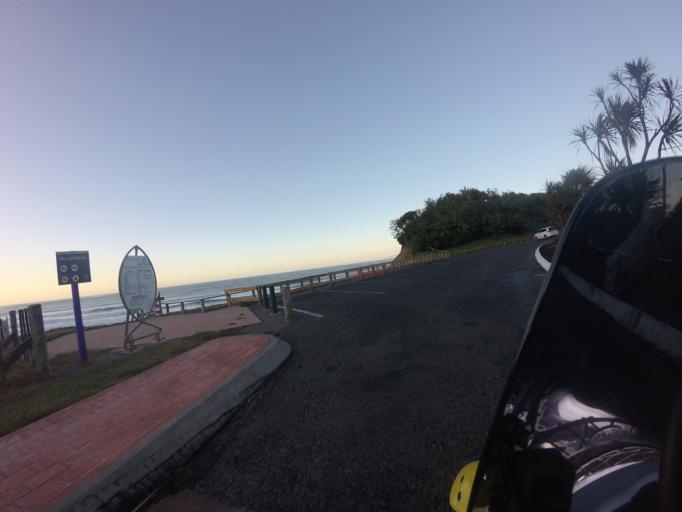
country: NZ
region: Gisborne
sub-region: Gisborne District
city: Gisborne
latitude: -38.6993
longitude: 178.0574
